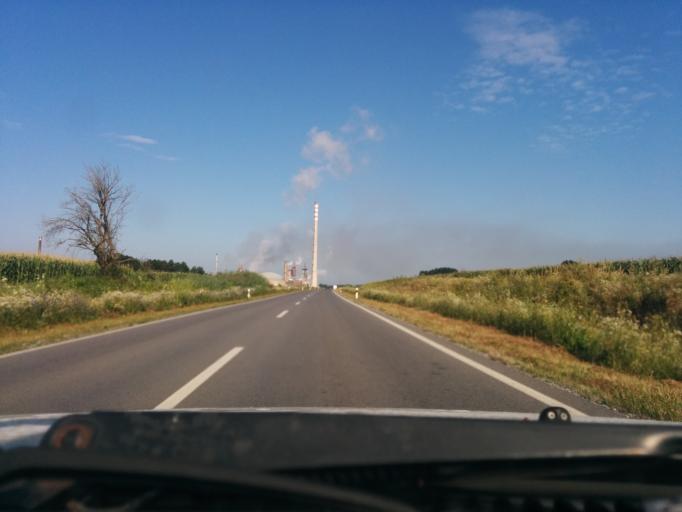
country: HR
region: Sisacko-Moslavacka
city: Husain
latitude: 45.4626
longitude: 16.8184
